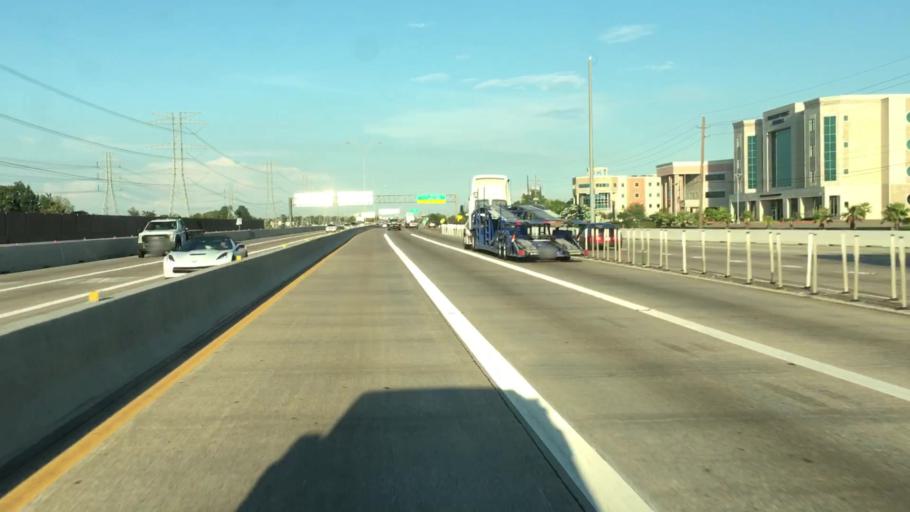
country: US
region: Texas
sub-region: Harris County
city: Hudson
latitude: 29.9376
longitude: -95.4701
